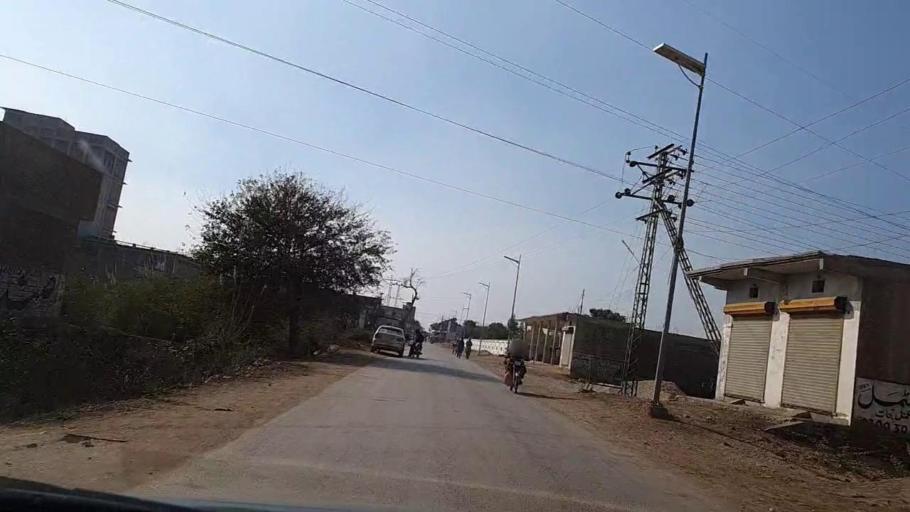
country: PK
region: Sindh
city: Sakrand
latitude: 26.1380
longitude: 68.2629
